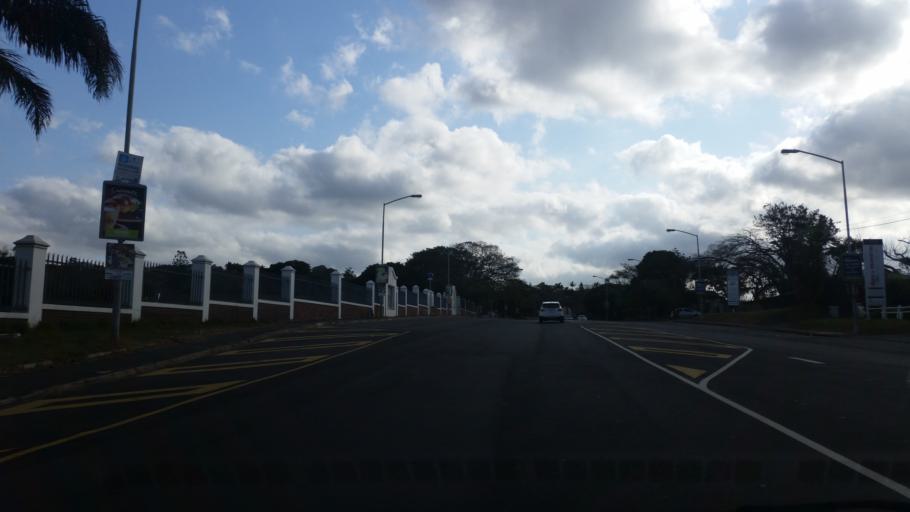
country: ZA
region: KwaZulu-Natal
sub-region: eThekwini Metropolitan Municipality
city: Berea
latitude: -29.8276
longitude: 30.9290
